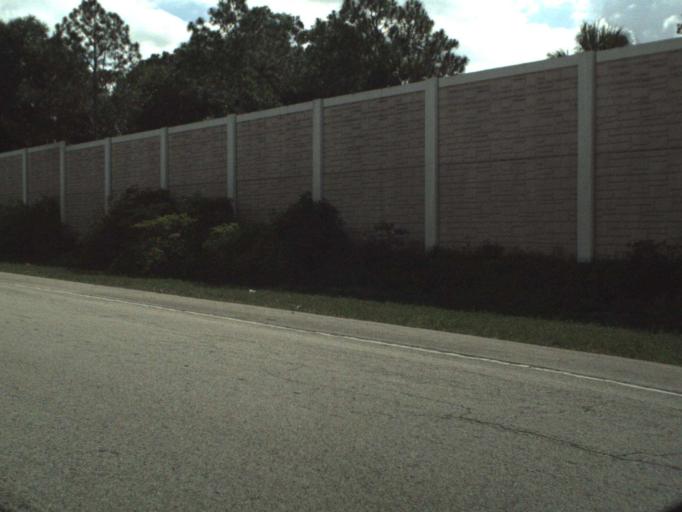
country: US
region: Florida
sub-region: Seminole County
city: Wekiwa Springs
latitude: 28.6956
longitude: -81.3873
